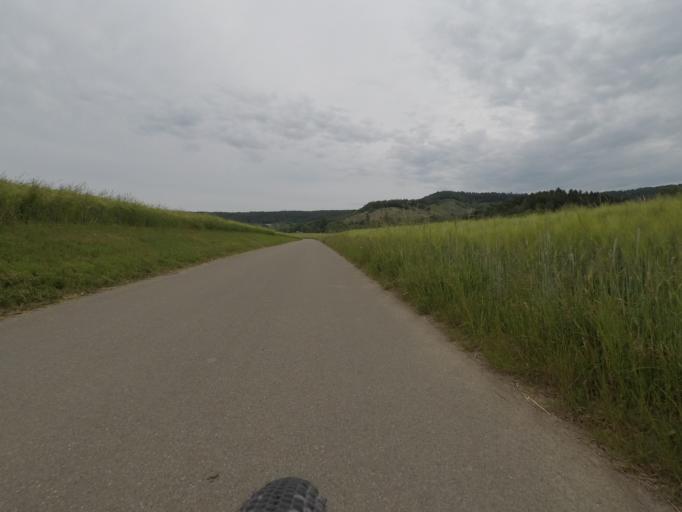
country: DE
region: Baden-Wuerttemberg
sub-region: Regierungsbezirk Stuttgart
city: Hildrizhausen
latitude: 48.5630
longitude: 8.9625
